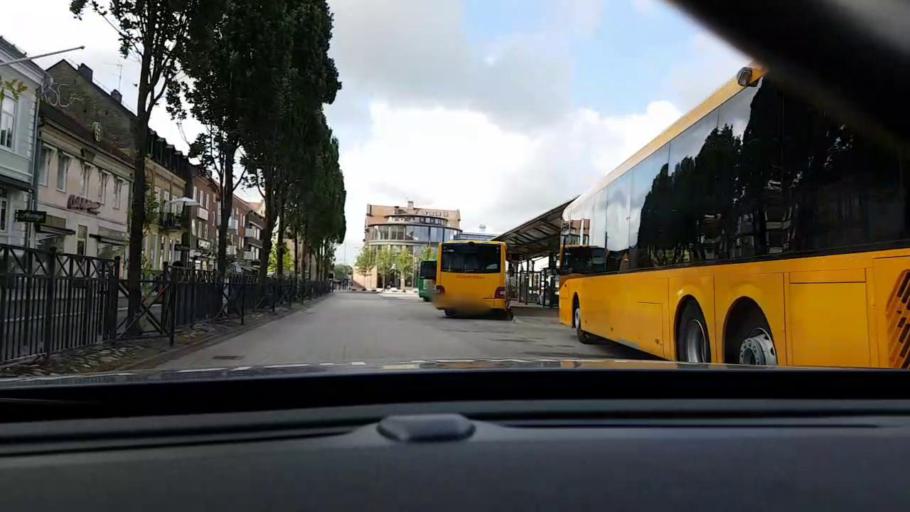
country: SE
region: Skane
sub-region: Hassleholms Kommun
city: Hassleholm
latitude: 56.1591
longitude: 13.7645
